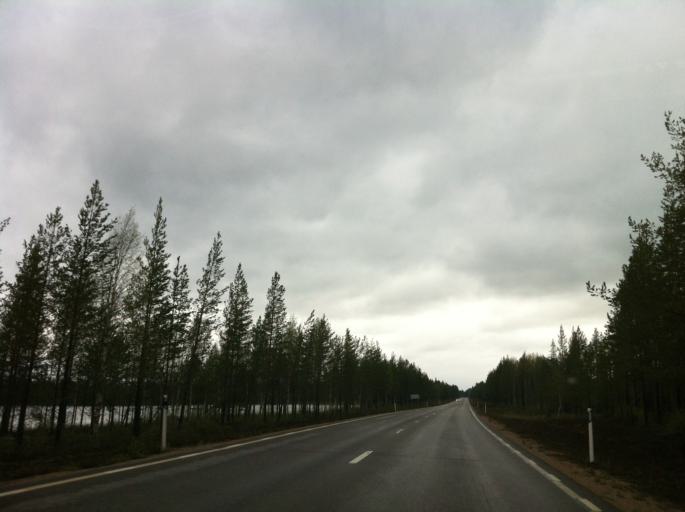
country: SE
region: Jaemtland
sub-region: Harjedalens Kommun
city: Sveg
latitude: 62.1249
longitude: 14.1192
